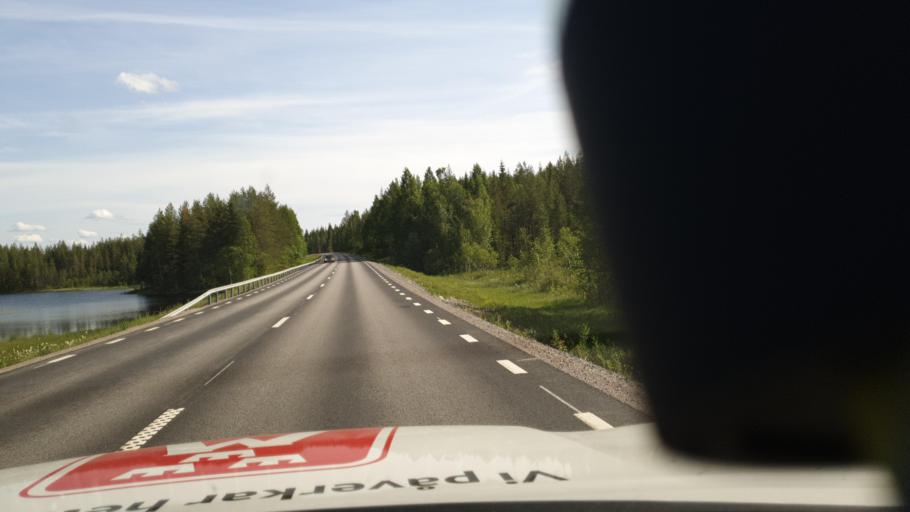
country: SE
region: Vaesterbotten
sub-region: Skelleftea Kommun
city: Boliden
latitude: 64.8945
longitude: 20.3744
